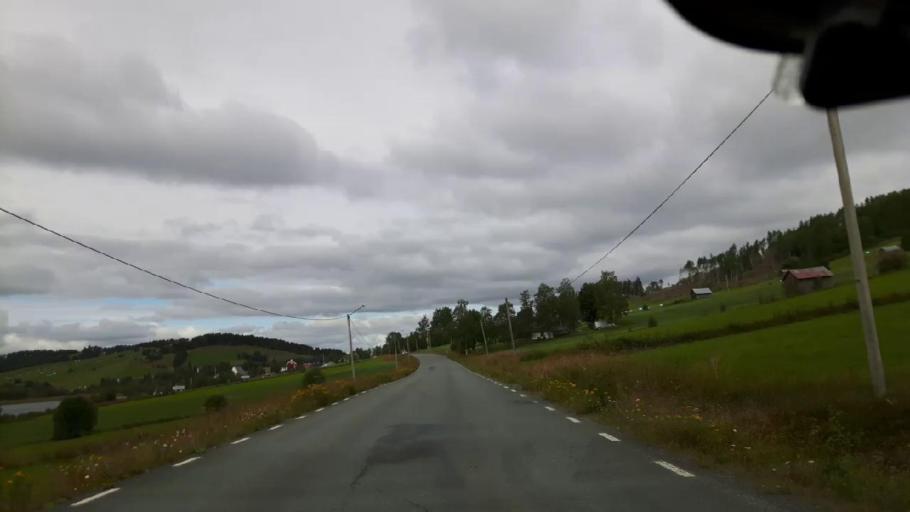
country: SE
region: Jaemtland
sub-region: Krokoms Kommun
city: Valla
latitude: 63.4886
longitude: 13.9154
